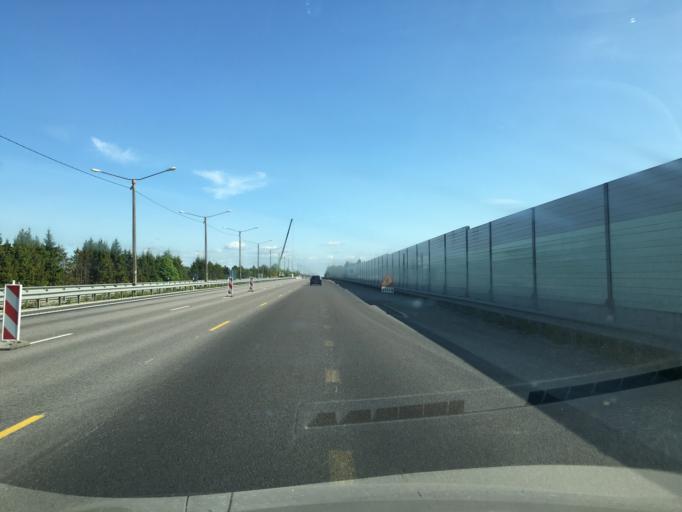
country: EE
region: Harju
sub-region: Rae vald
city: Jueri
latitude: 59.3805
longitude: 24.8401
